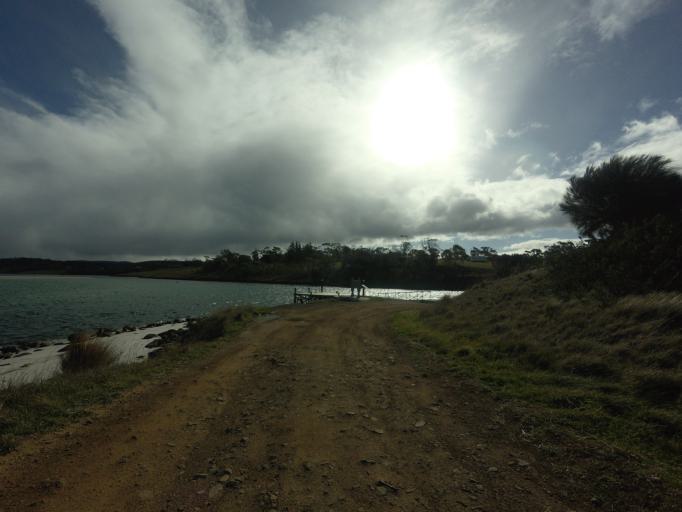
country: AU
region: Tasmania
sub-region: Sorell
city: Sorell
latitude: -42.3102
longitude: 147.9950
